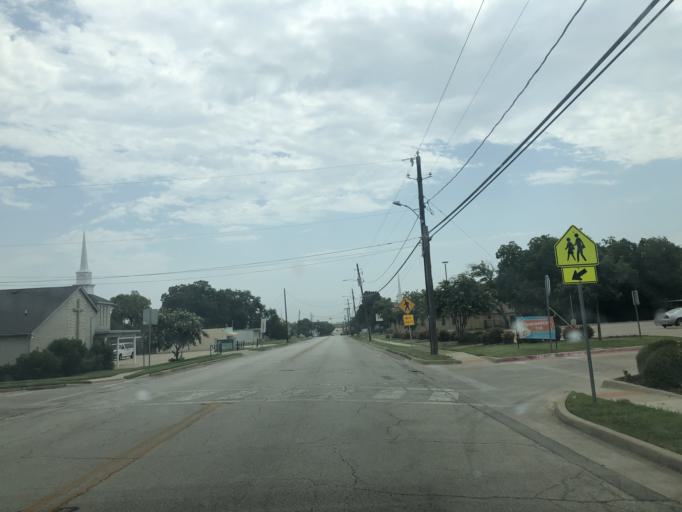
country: US
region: Texas
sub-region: Dallas County
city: Grand Prairie
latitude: 32.7350
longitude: -97.0313
